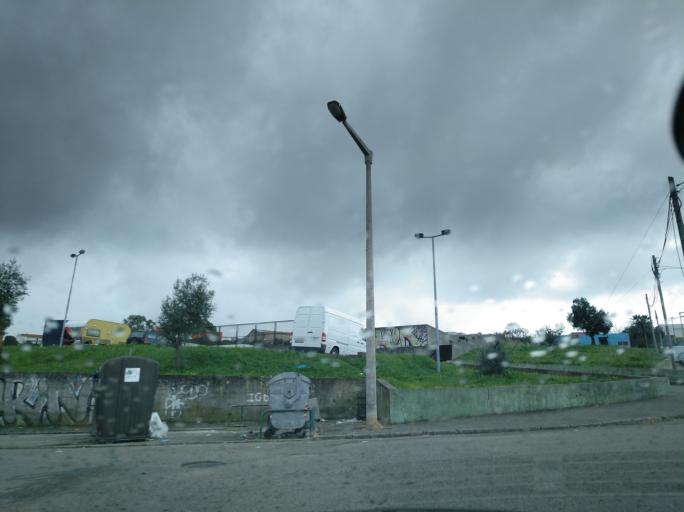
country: PT
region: Lisbon
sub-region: Odivelas
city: Pontinha
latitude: 38.7702
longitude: -9.2050
